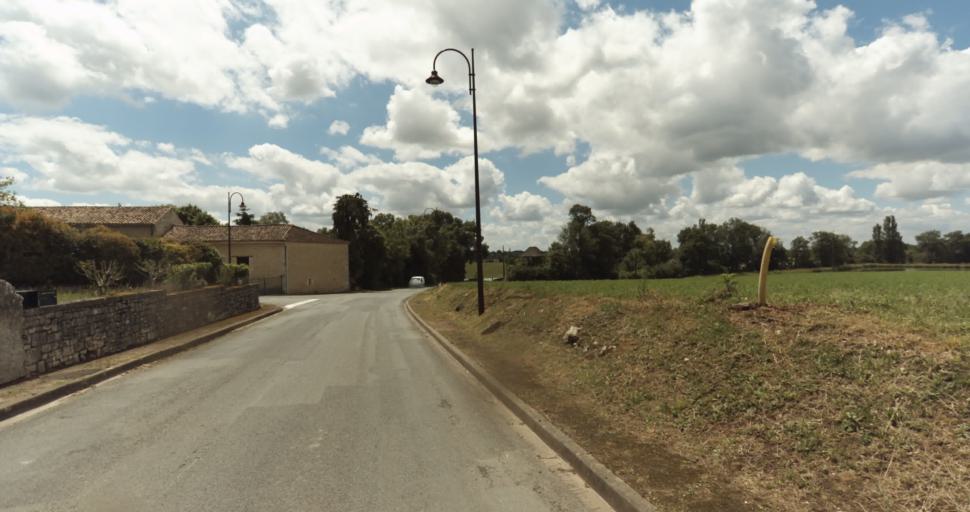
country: FR
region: Aquitaine
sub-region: Departement de la Dordogne
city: Beaumont-du-Perigord
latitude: 44.7246
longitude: 0.7584
